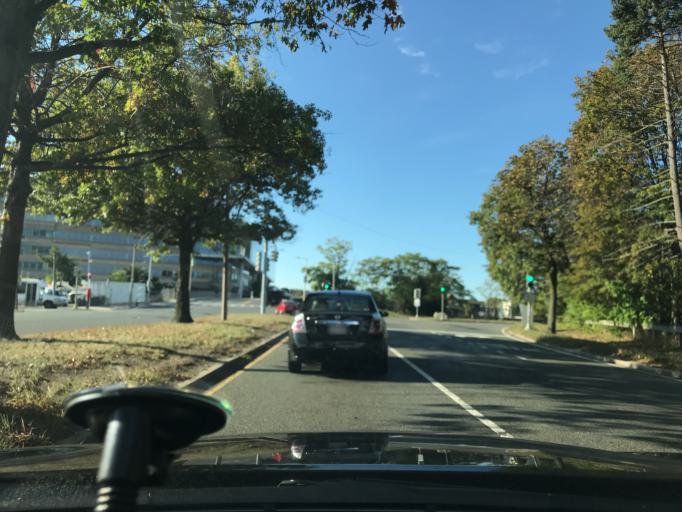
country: US
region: Massachusetts
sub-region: Middlesex County
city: Watertown
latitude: 42.3594
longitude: -71.1473
